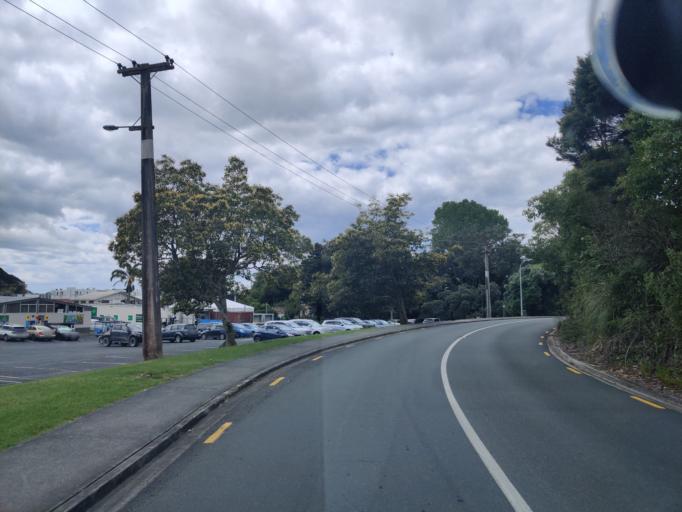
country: NZ
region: Northland
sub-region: Far North District
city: Paihia
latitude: -35.2831
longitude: 174.0915
